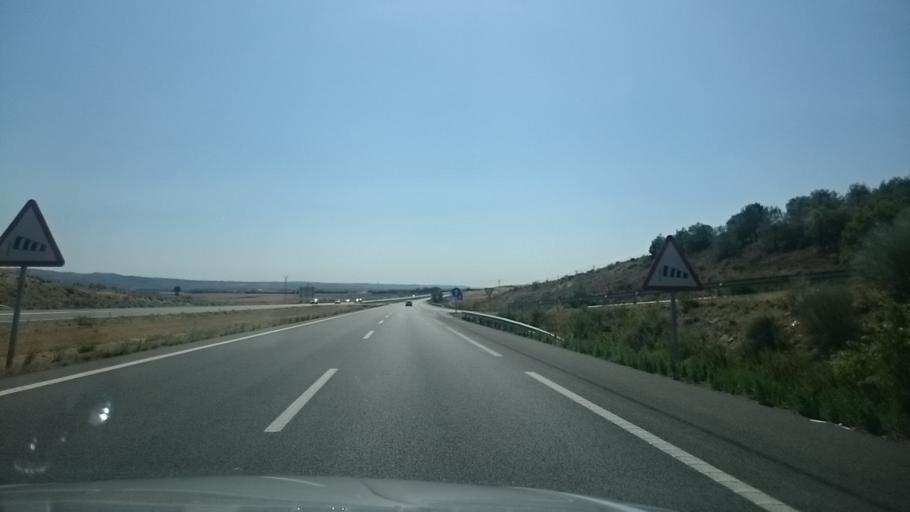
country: ES
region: Aragon
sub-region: Provincia de Zaragoza
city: Gallur
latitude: 41.8331
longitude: -1.3176
